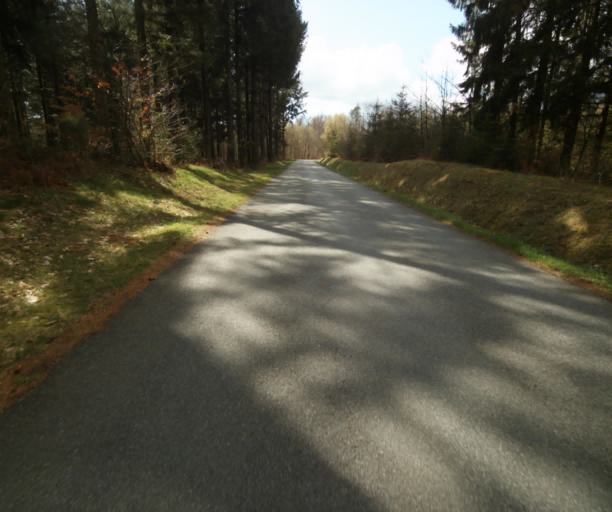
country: FR
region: Limousin
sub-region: Departement de la Correze
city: Argentat
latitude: 45.2341
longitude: 1.9351
